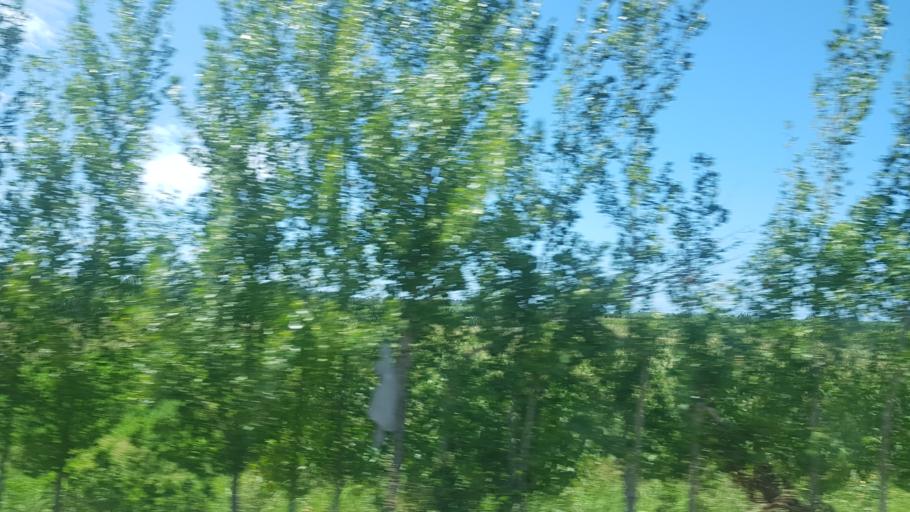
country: AL
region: Fier
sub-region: Rrethi i Fierit
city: Frakulla e Madhe
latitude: 40.6188
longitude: 19.5185
